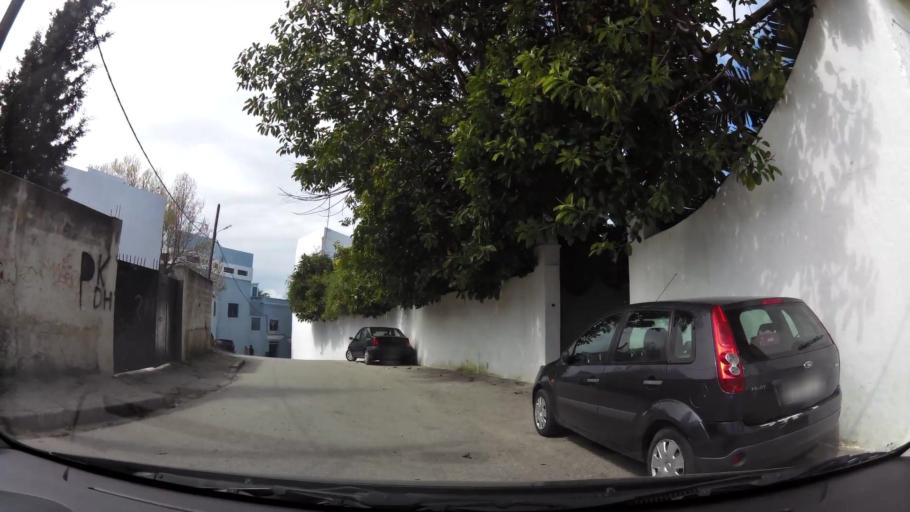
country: MA
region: Tanger-Tetouan
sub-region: Tanger-Assilah
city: Tangier
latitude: 35.7891
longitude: -5.8160
